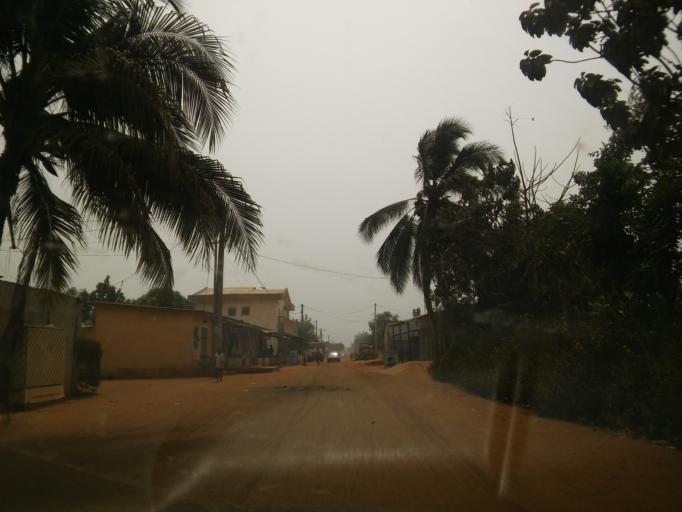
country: BJ
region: Mono
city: Come
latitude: 6.4097
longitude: 1.8772
